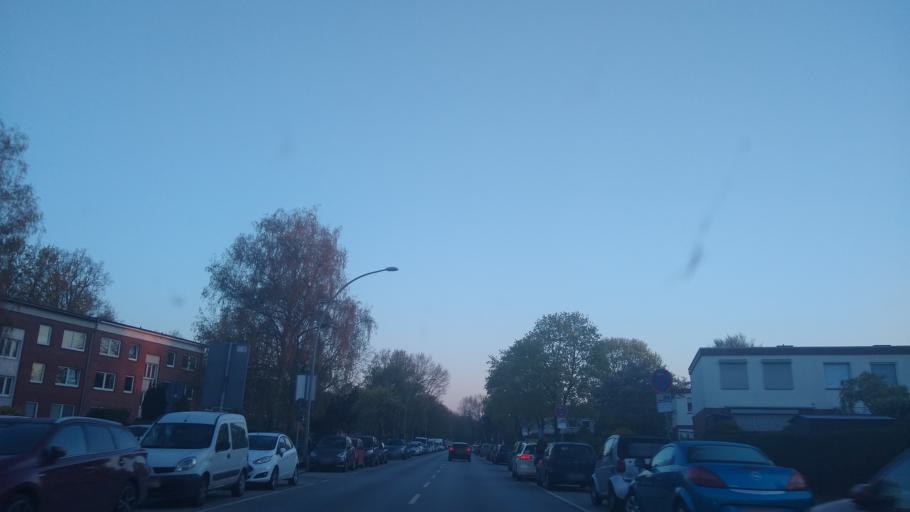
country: DE
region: Schleswig-Holstein
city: Bonningstedt
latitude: 53.6387
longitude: 9.9188
